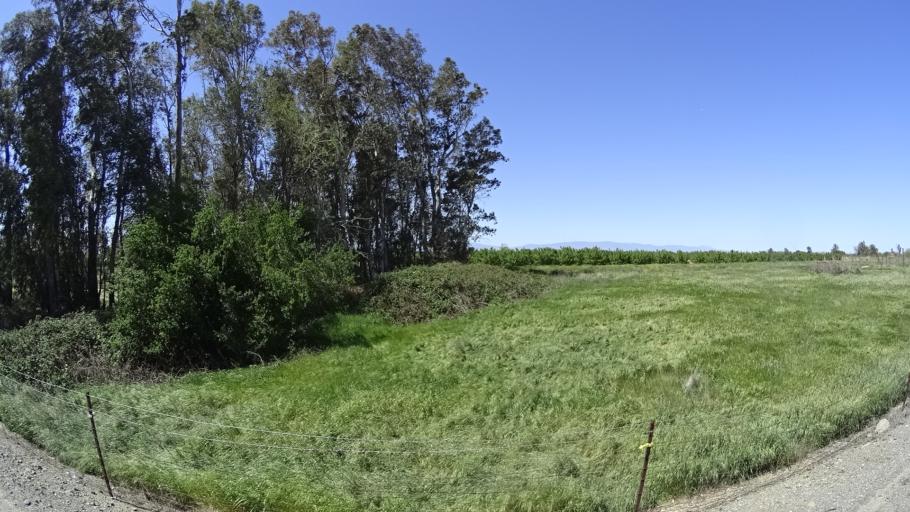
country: US
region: California
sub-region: Glenn County
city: Orland
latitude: 39.7887
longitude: -122.1858
